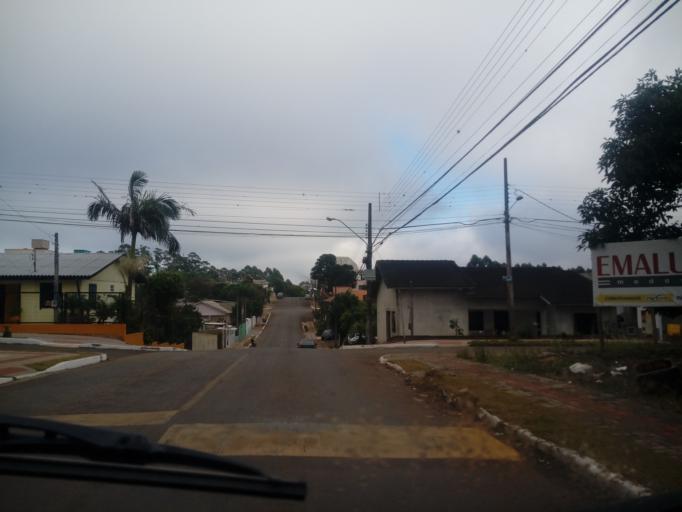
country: BR
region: Santa Catarina
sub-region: Chapeco
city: Chapeco
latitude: -27.1163
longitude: -52.6270
